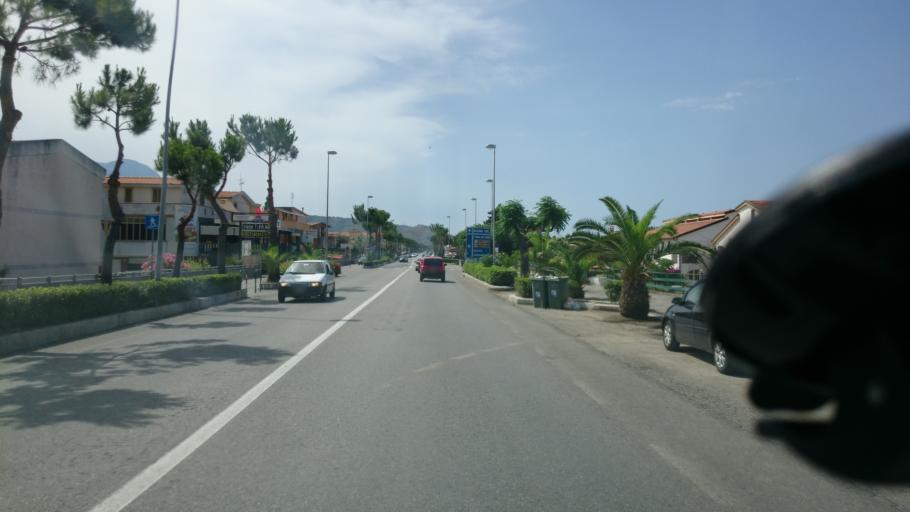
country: IT
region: Calabria
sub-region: Provincia di Cosenza
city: Marcellina
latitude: 39.7559
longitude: 15.8036
